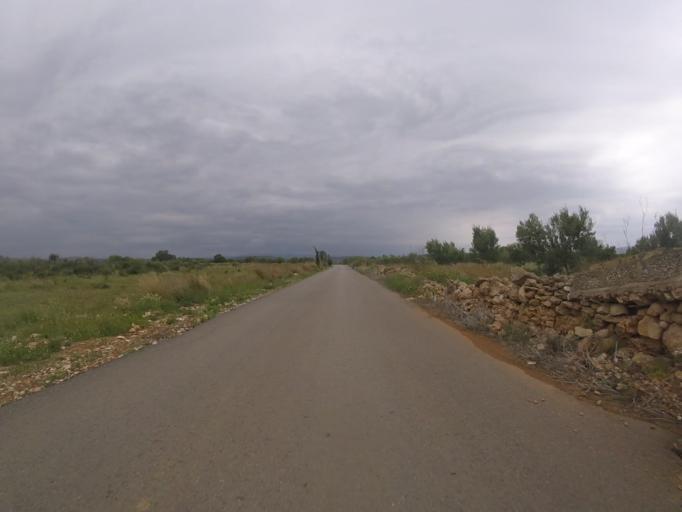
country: ES
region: Valencia
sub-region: Provincia de Castello
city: Torreblanca
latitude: 40.2134
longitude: 0.2473
